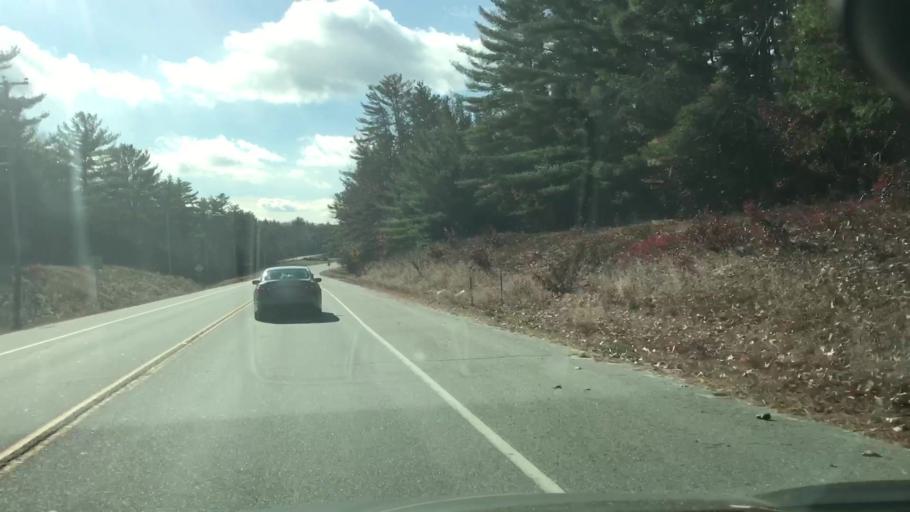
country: US
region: New Hampshire
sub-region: Belknap County
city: Barnstead
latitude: 43.3481
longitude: -71.2646
